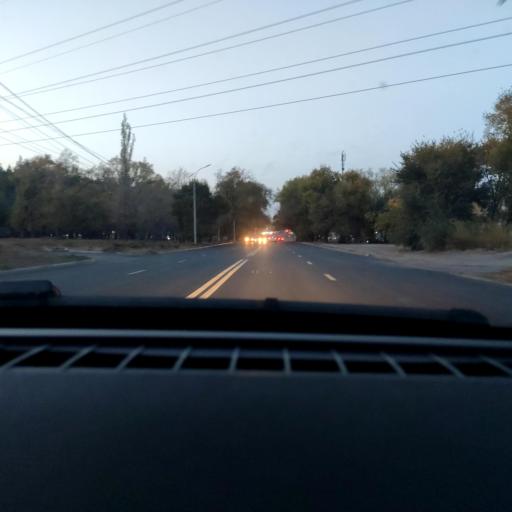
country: RU
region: Voronezj
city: Maslovka
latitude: 51.5979
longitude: 39.2438
